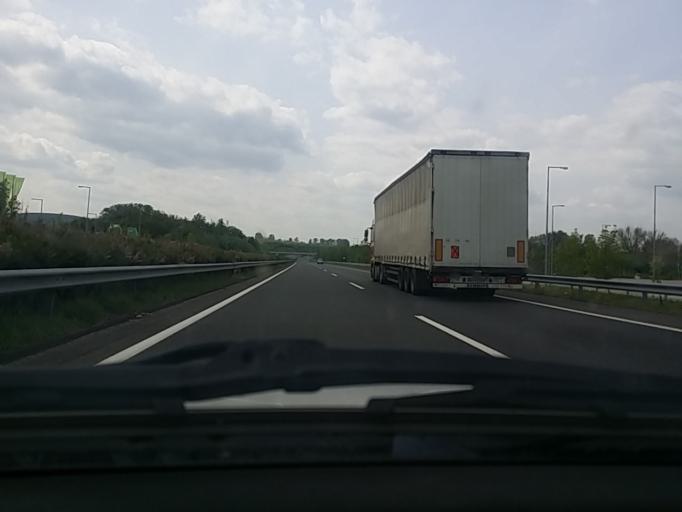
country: HU
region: Somogy
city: Balatonlelle
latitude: 46.7767
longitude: 17.7211
